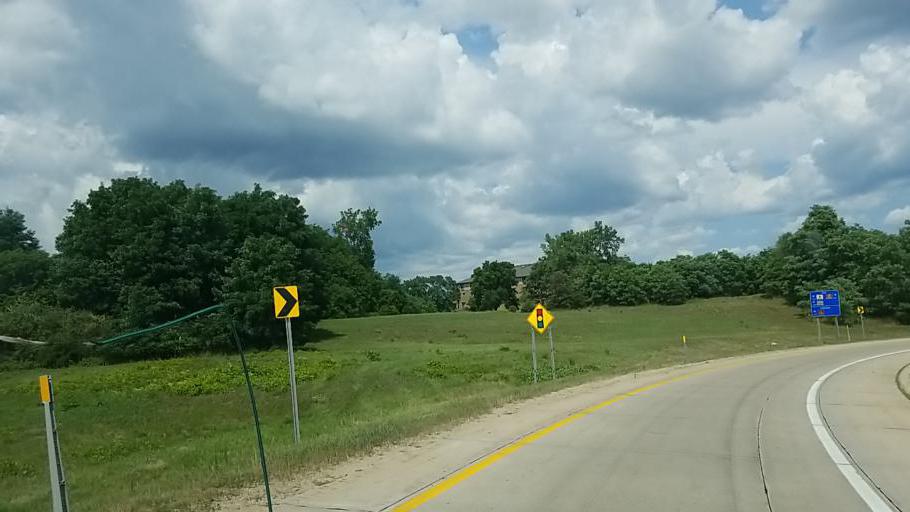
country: US
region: Michigan
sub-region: Kent County
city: Comstock Park
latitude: 43.0442
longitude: -85.6616
